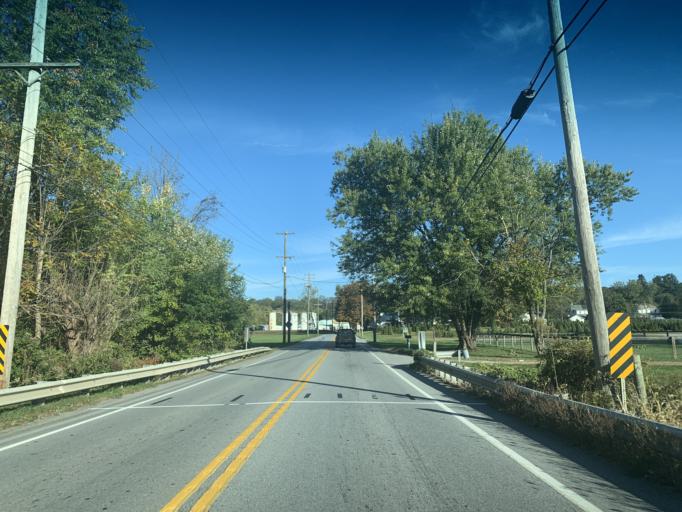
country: US
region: Pennsylvania
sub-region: Chester County
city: Parkesburg
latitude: 39.9561
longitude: -75.9120
